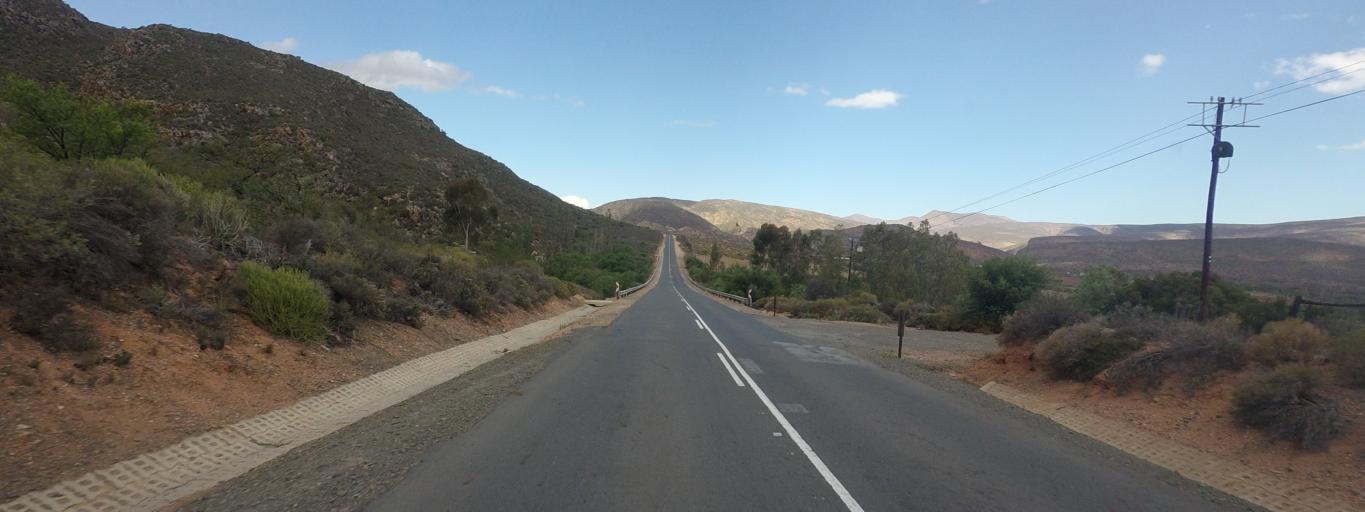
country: ZA
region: Western Cape
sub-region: Eden District Municipality
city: Ladismith
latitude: -33.4712
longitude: 21.4943
